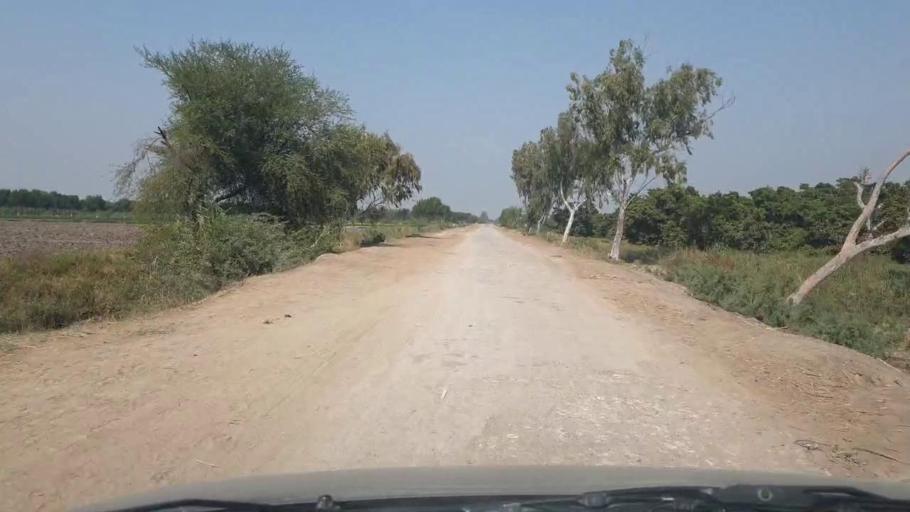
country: PK
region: Sindh
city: Mirwah Gorchani
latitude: 25.3601
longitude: 69.1447
